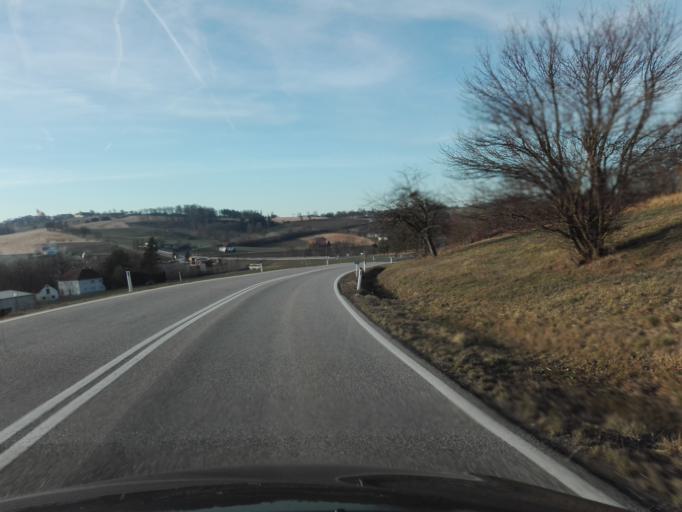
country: AT
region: Lower Austria
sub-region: Politischer Bezirk Amstetten
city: Strengberg
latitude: 48.1378
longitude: 14.6763
